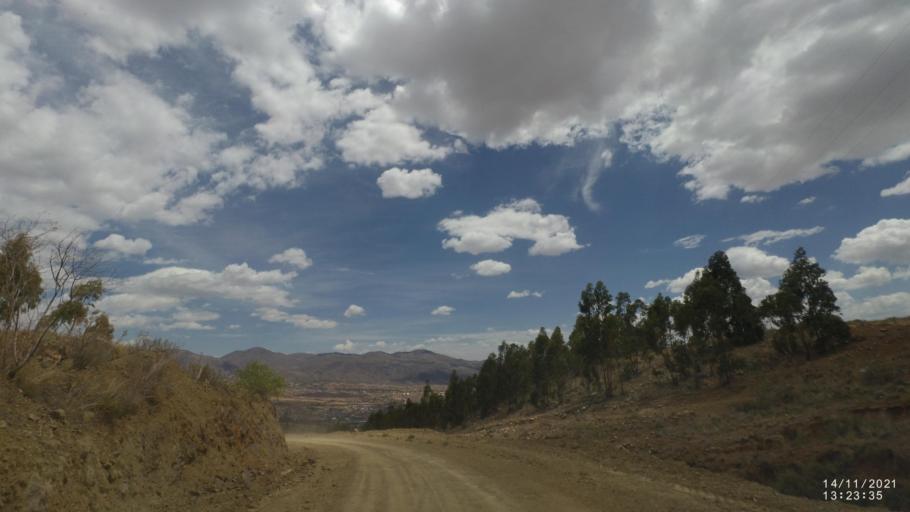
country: BO
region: Cochabamba
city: Colomi
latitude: -17.3766
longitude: -65.9826
